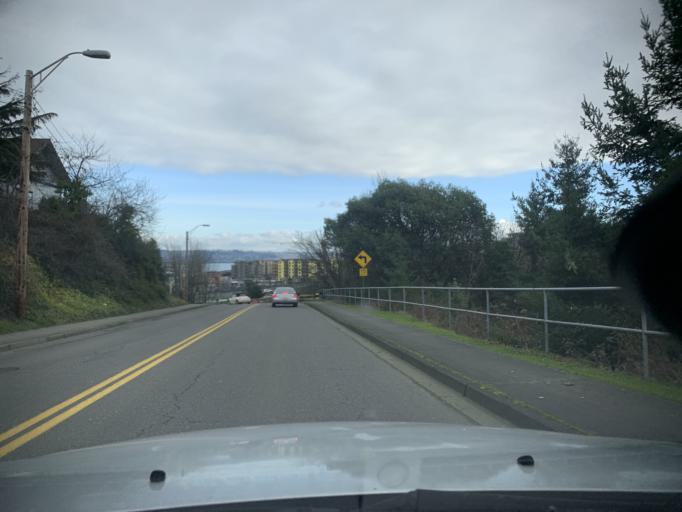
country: US
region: Washington
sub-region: Pierce County
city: Fircrest
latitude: 47.2982
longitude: -122.5111
